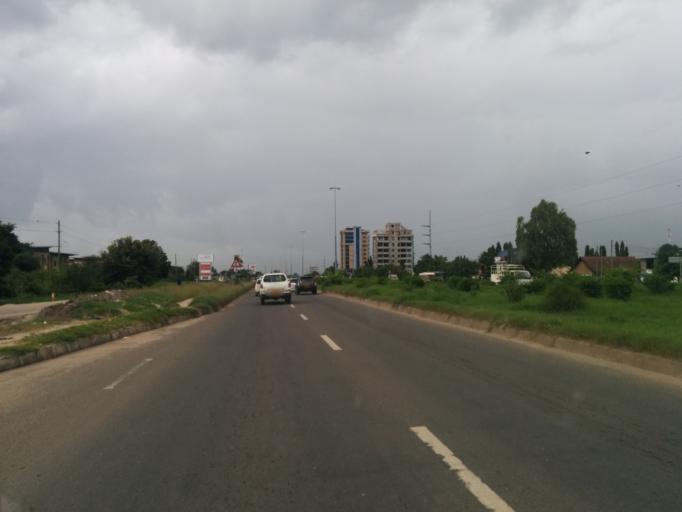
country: TZ
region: Dar es Salaam
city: Magomeni
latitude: -6.7777
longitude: 39.2181
